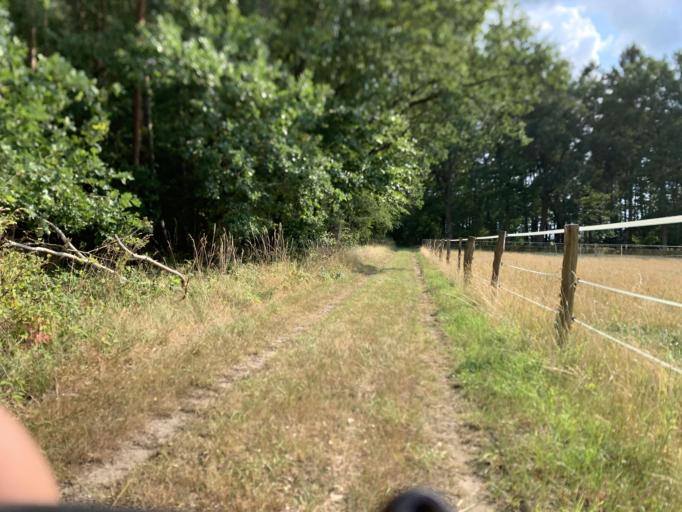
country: DE
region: Lower Saxony
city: Thomasburg
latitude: 53.2407
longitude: 10.6386
